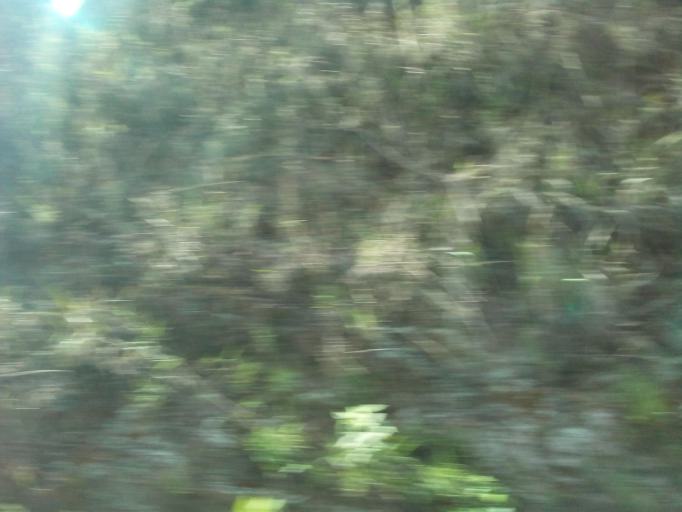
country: BR
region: Minas Gerais
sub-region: Caete
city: Caete
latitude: -19.8886
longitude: -43.7546
